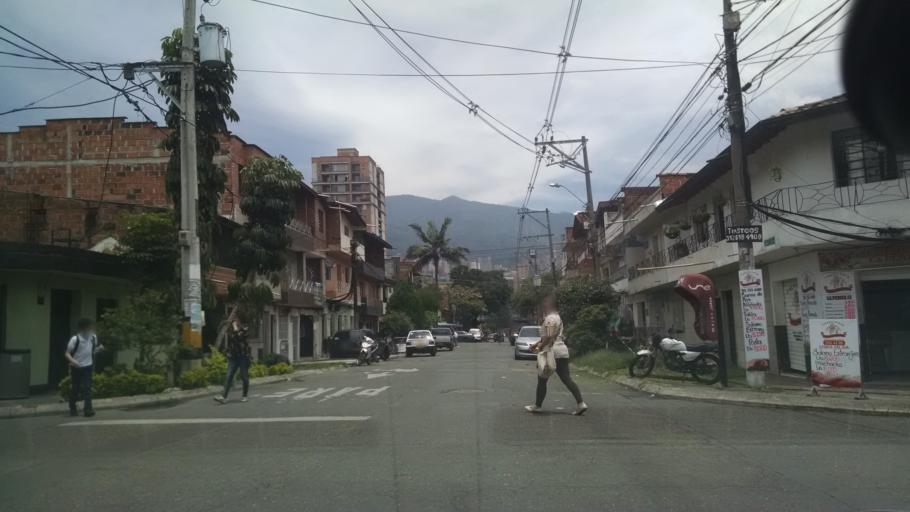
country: CO
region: Antioquia
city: Itagui
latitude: 6.2055
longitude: -75.5851
